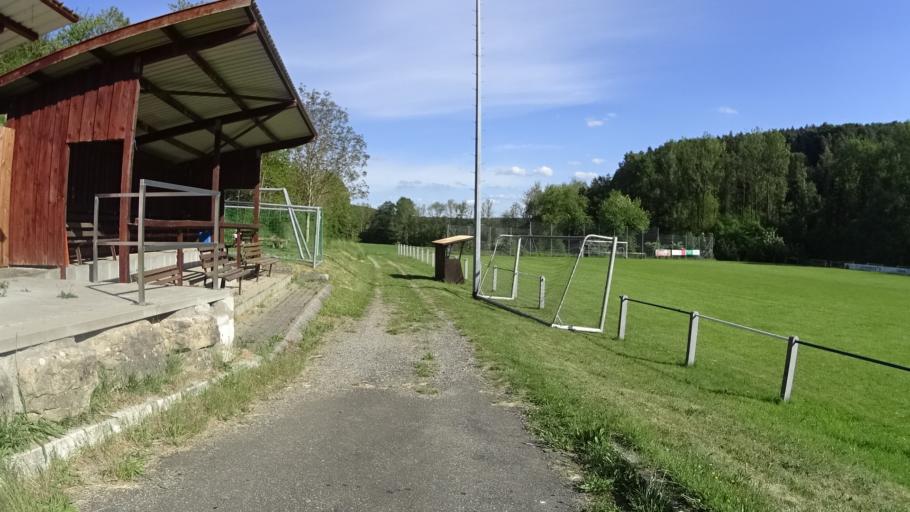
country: DE
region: Baden-Wuerttemberg
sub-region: Regierungsbezirk Stuttgart
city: Boxberg
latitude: 49.4975
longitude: 9.6034
